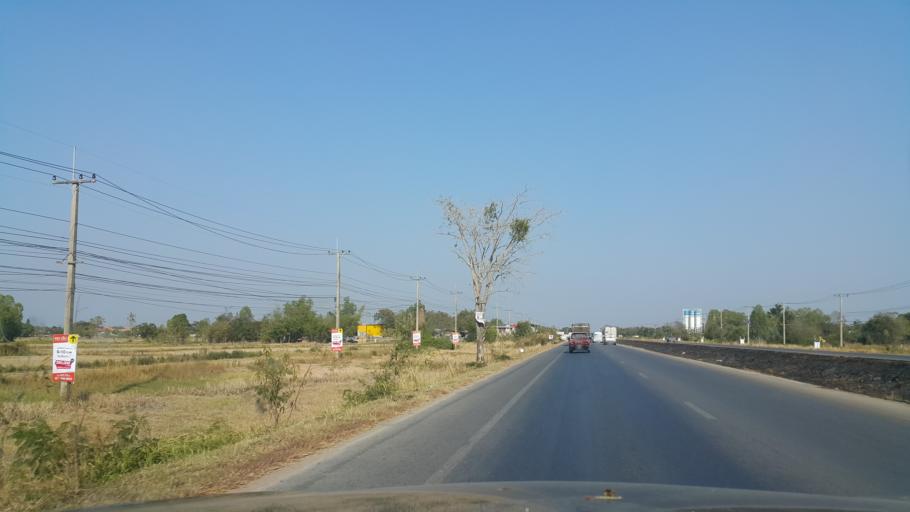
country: TH
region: Khon Kaen
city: Khon Kaen
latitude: 16.4012
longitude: 102.8722
